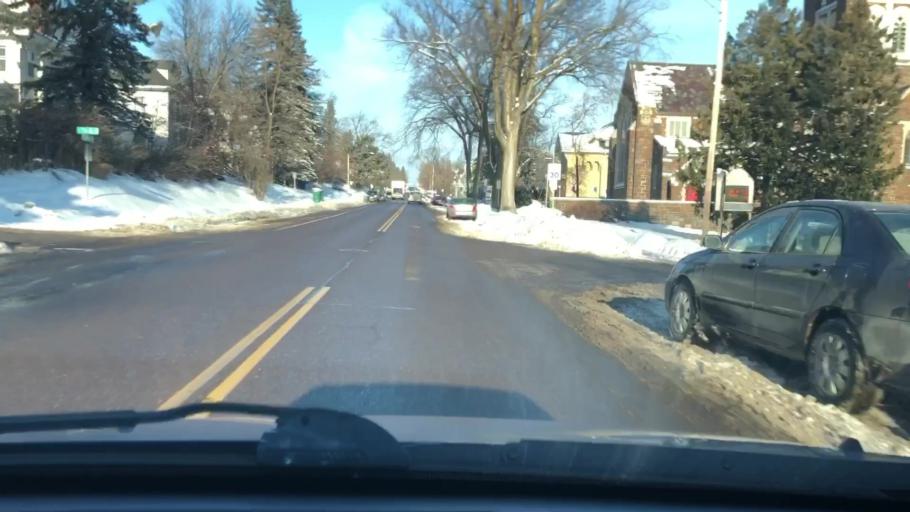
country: US
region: Minnesota
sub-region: Saint Louis County
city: Duluth
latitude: 46.8030
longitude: -92.0772
